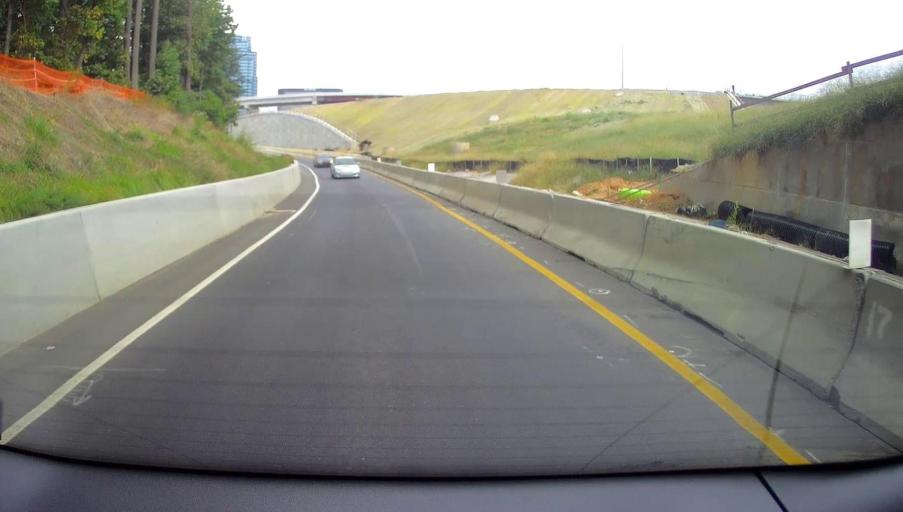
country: US
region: Georgia
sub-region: Fulton County
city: Sandy Springs
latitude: 33.9119
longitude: -84.3595
